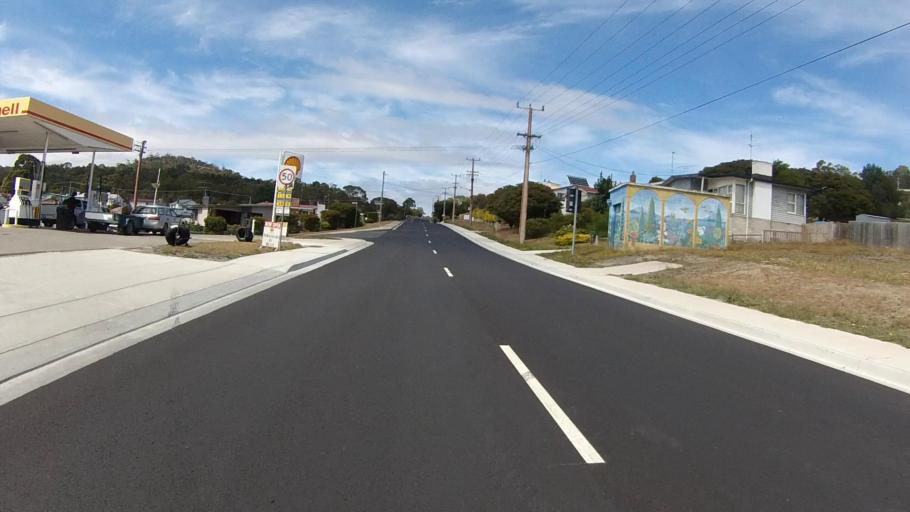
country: AU
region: Tasmania
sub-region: Clarence
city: Lindisfarne
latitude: -42.8130
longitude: 147.3513
